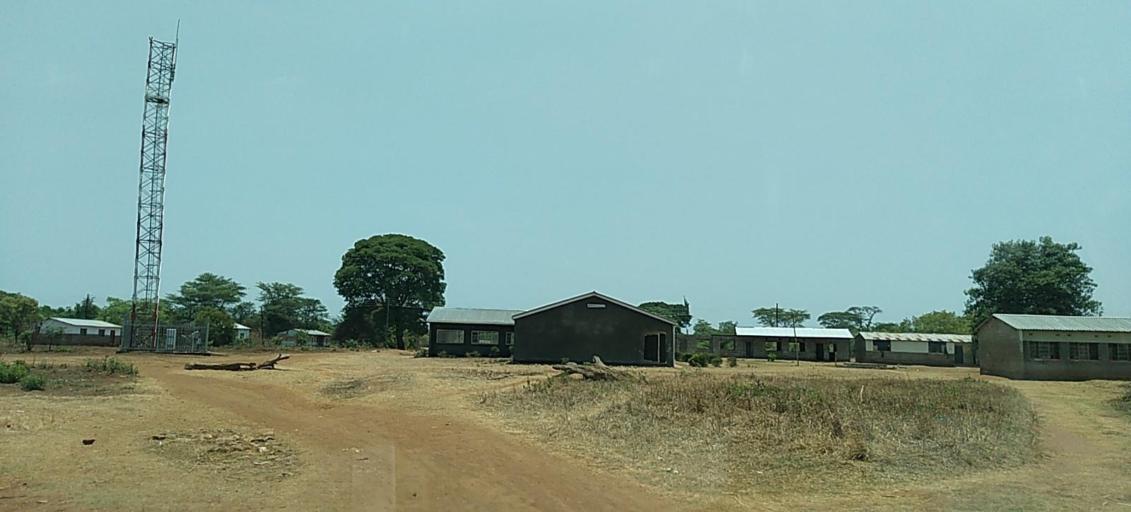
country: ZM
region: Copperbelt
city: Mpongwe
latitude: -13.8343
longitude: 27.8380
